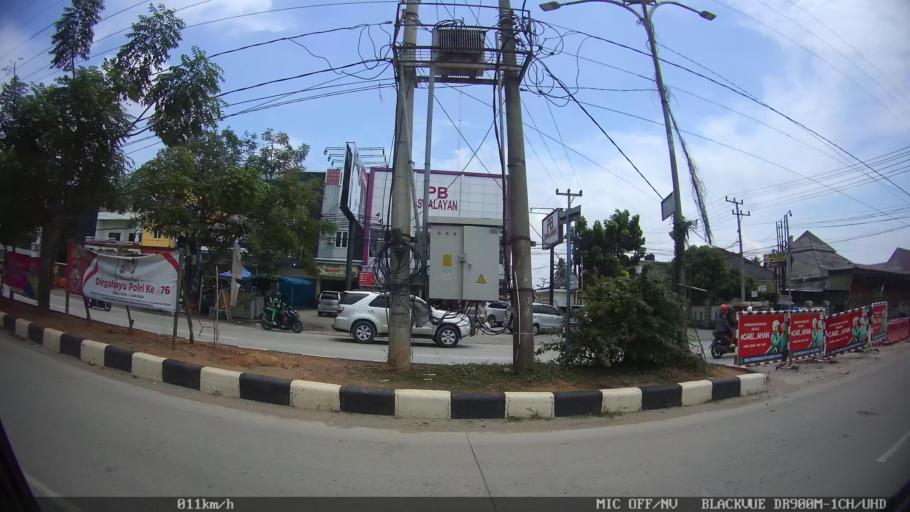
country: ID
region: Lampung
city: Kedaton
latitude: -5.3608
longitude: 105.3045
